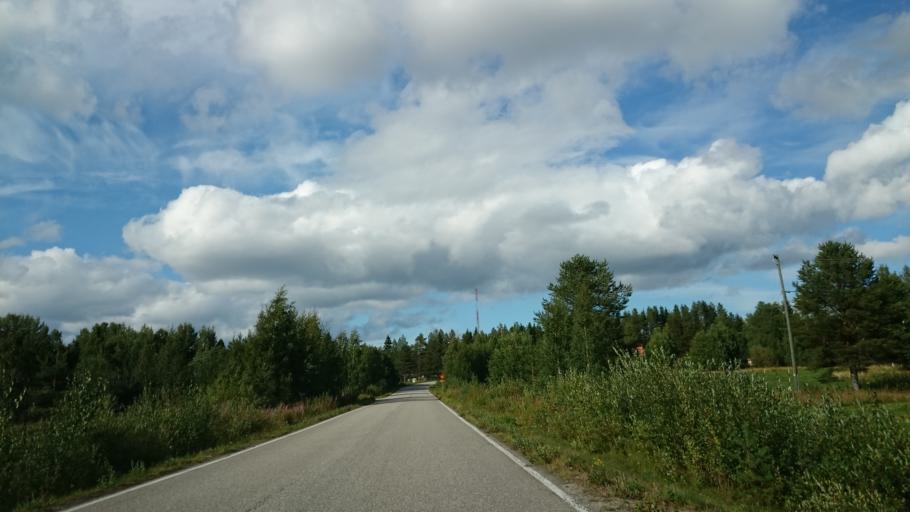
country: FI
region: Kainuu
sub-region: Kehys-Kainuu
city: Suomussalmi
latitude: 64.7450
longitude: 29.4398
